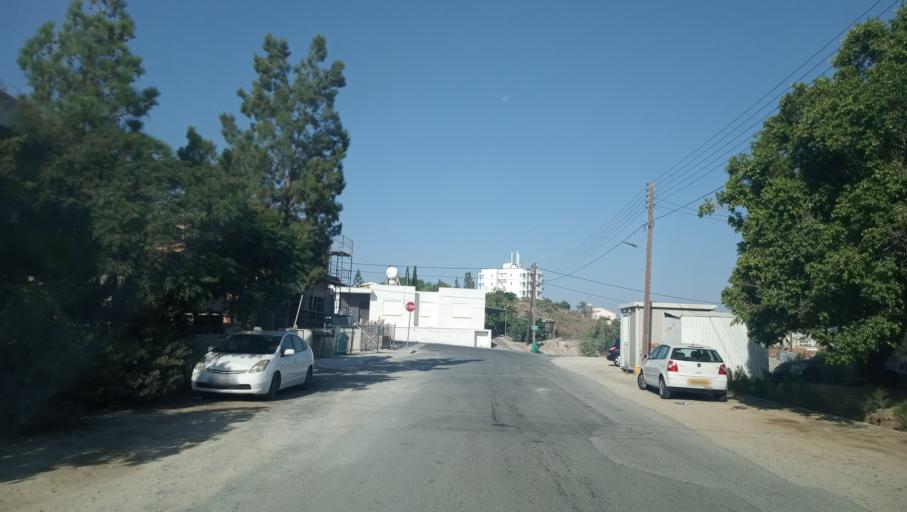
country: CY
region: Lefkosia
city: Geri
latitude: 35.1039
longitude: 33.4251
